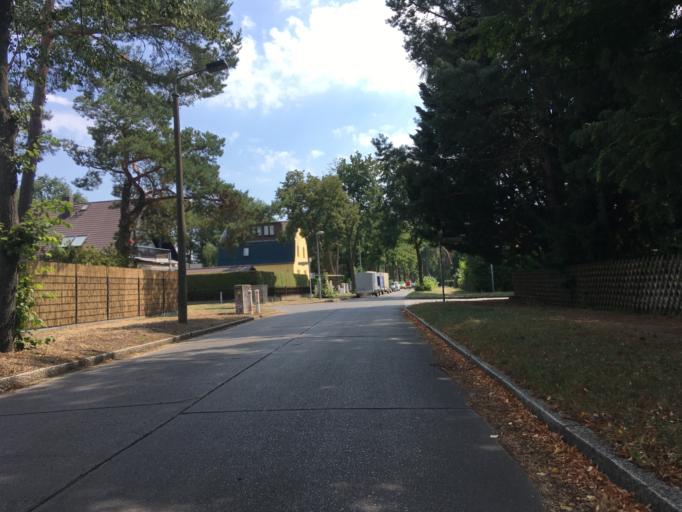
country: DE
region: Berlin
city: Mahlsdorf
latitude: 52.4881
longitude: 13.6133
